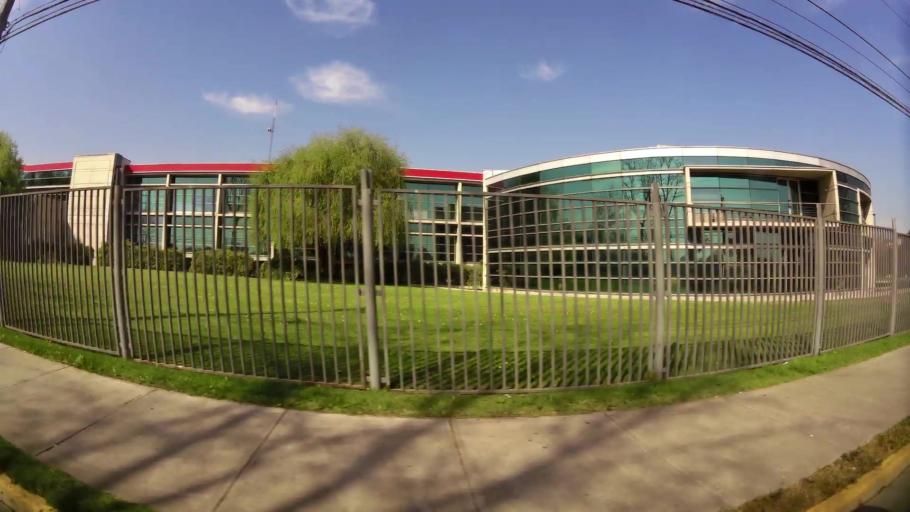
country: CL
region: Santiago Metropolitan
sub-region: Provincia de Santiago
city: Lo Prado
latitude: -33.4548
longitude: -70.7365
